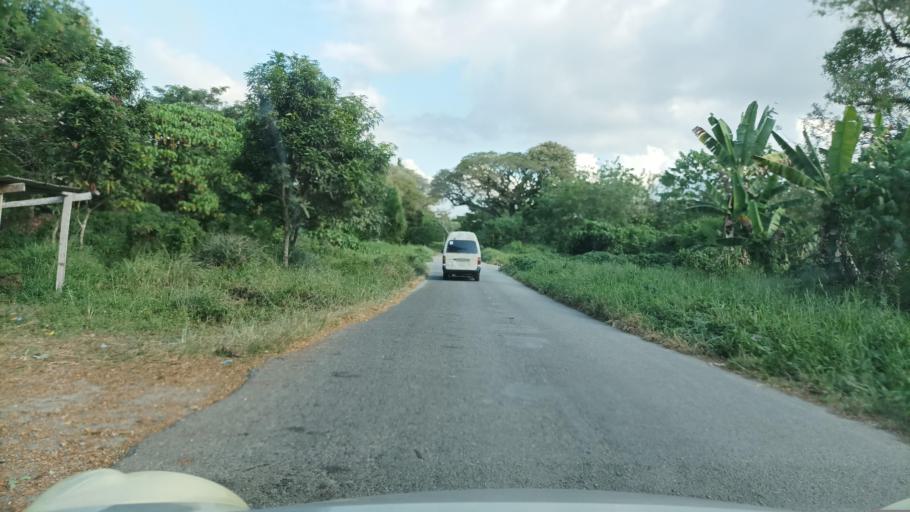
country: SB
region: Guadalcanal
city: Honiara
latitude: -9.3177
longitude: 159.7984
